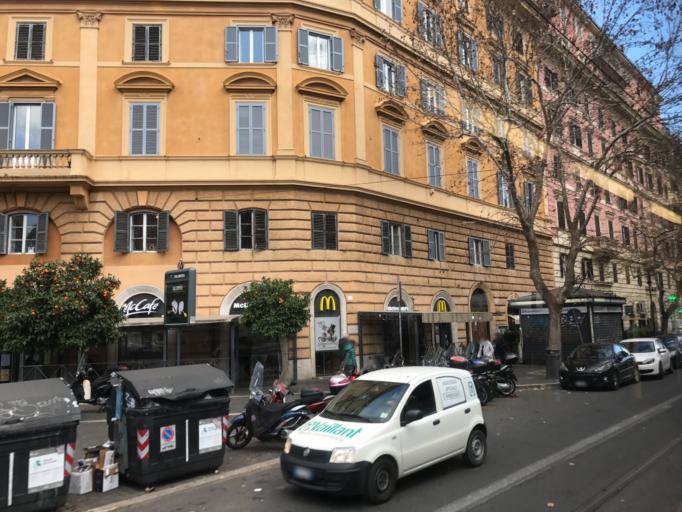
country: IT
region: Latium
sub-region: Citta metropolitana di Roma Capitale
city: Rome
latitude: 41.9139
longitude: 12.5054
